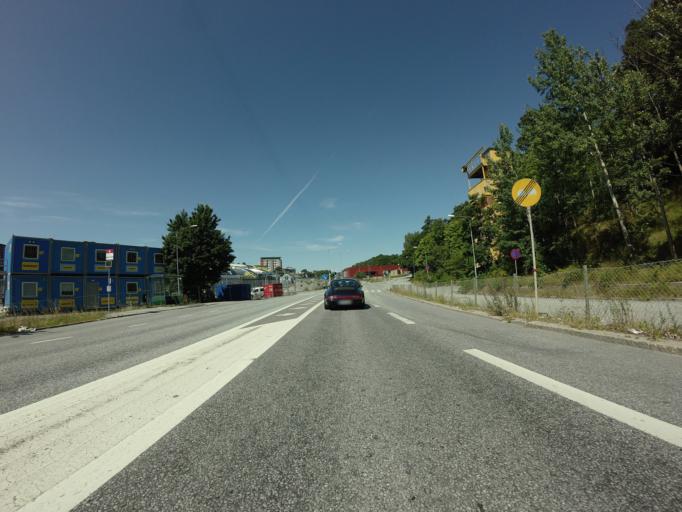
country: SE
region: Stockholm
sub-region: Lidingo
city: Lidingoe
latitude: 59.3469
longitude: 18.1558
